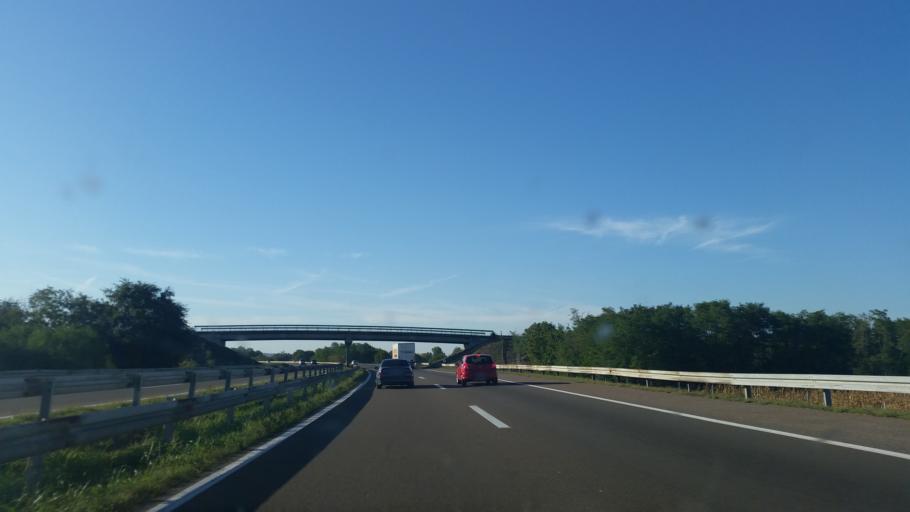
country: RS
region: Central Serbia
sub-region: Sumadijski Okrug
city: Batocina
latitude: 44.1081
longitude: 21.1649
